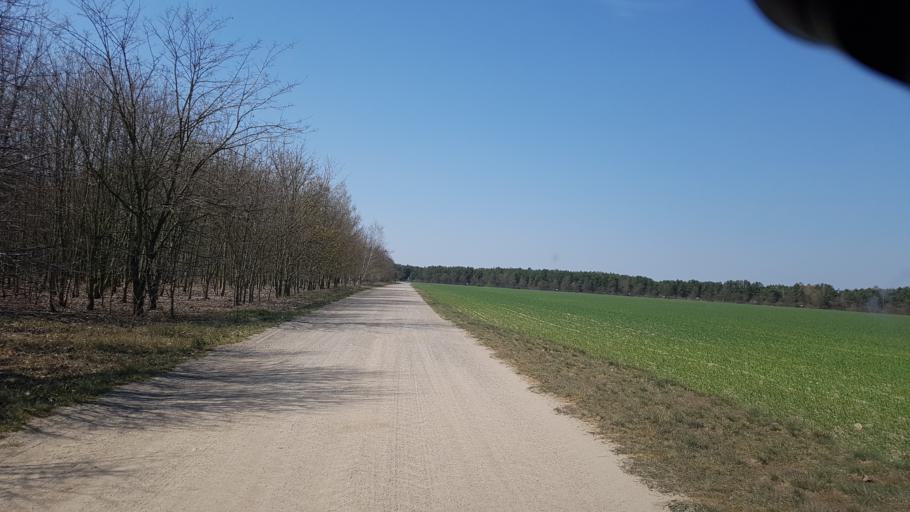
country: DE
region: Saxony-Anhalt
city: Holzdorf
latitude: 51.7582
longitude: 13.1917
